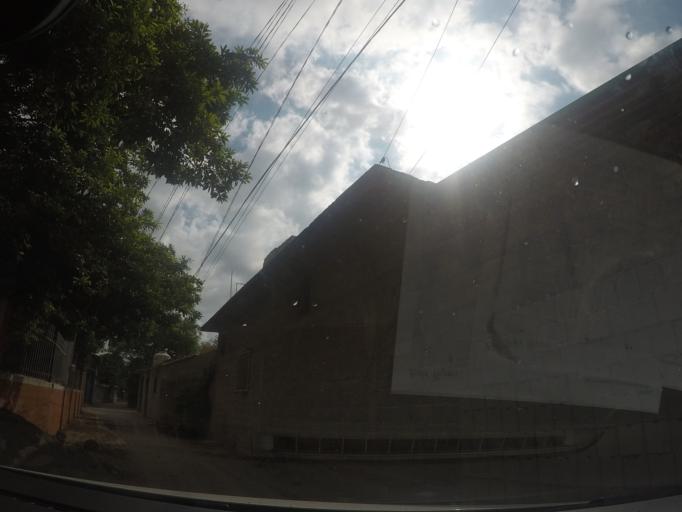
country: MX
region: Oaxaca
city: Juchitan de Zaragoza
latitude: 16.4292
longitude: -95.0300
